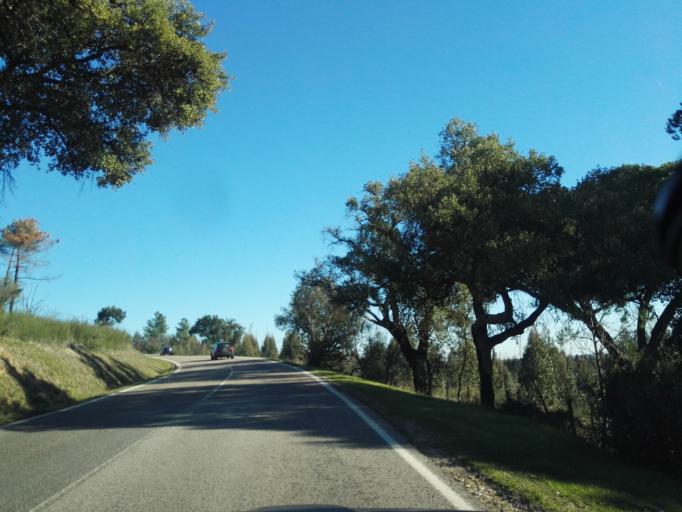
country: PT
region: Santarem
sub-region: Constancia
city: Constancia
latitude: 39.4808
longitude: -8.3195
